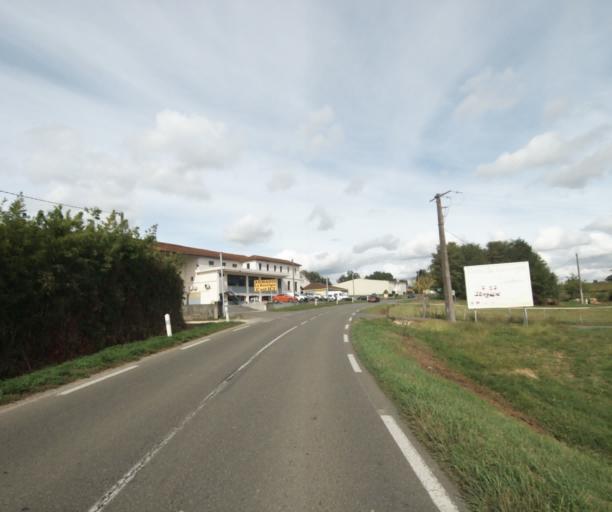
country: FR
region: Midi-Pyrenees
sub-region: Departement du Gers
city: Eauze
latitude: 43.8481
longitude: 0.0932
